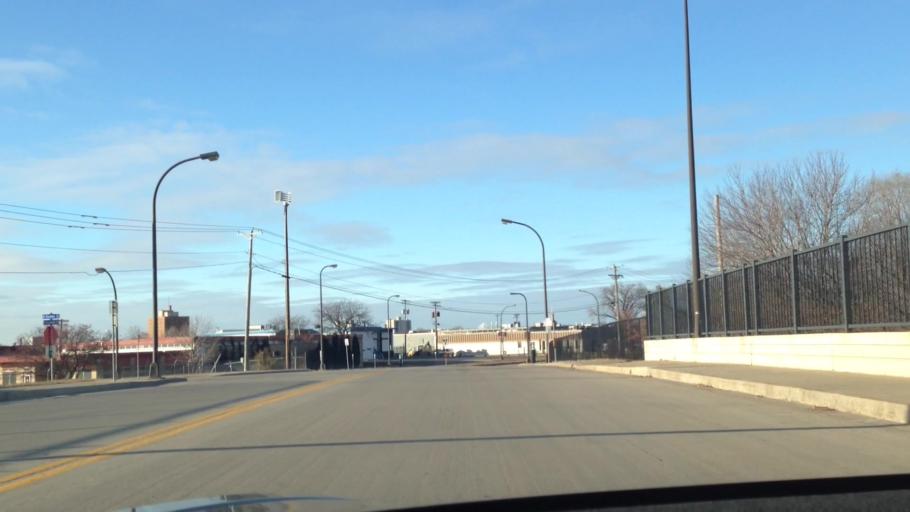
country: US
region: Minnesota
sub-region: Hennepin County
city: Minneapolis
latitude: 44.9798
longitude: -93.2821
